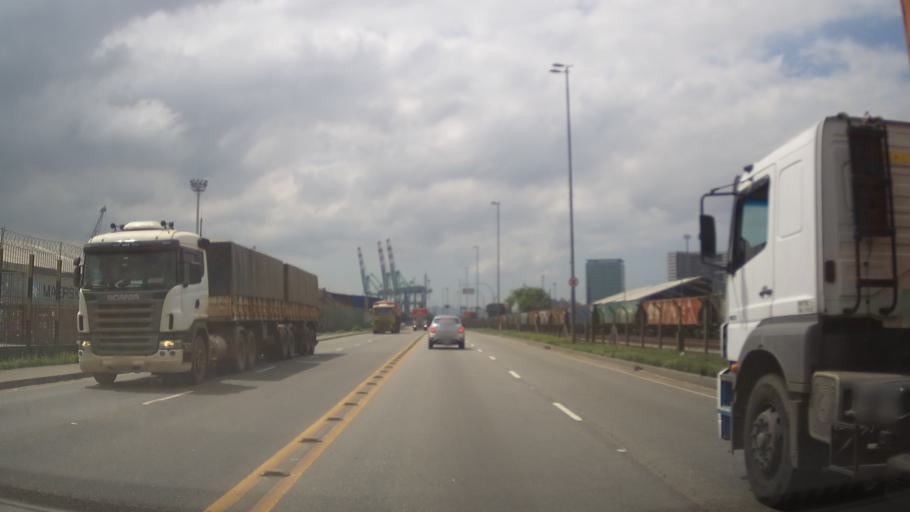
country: BR
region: Sao Paulo
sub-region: Santos
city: Santos
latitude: -23.9272
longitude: -46.3446
